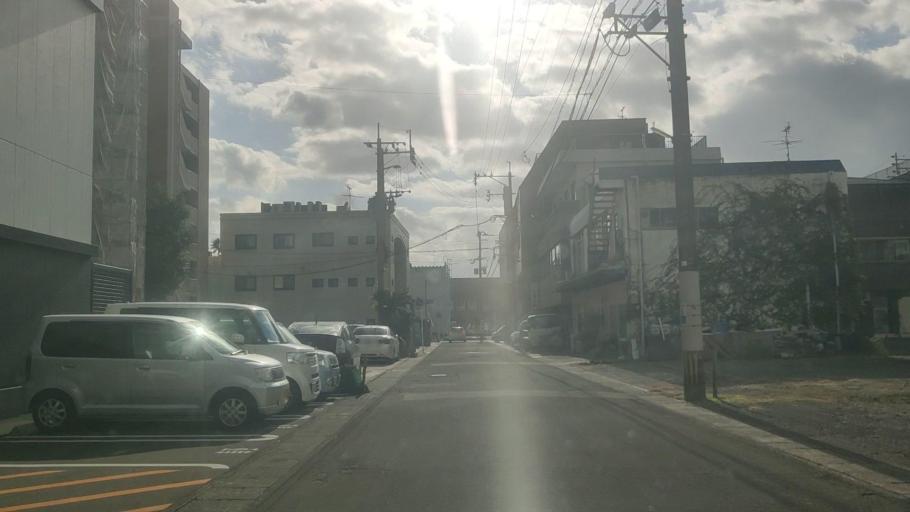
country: JP
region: Kagoshima
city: Kagoshima-shi
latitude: 31.6054
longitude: 130.5733
